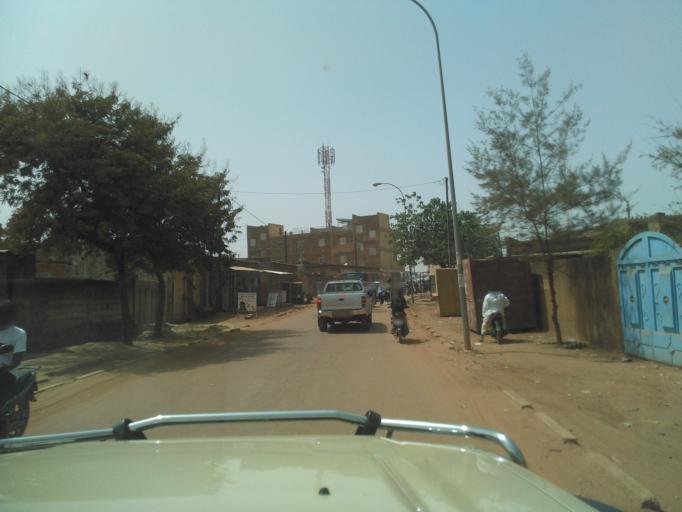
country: BF
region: Centre
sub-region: Kadiogo Province
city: Ouagadougou
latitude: 12.3967
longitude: -1.5551
